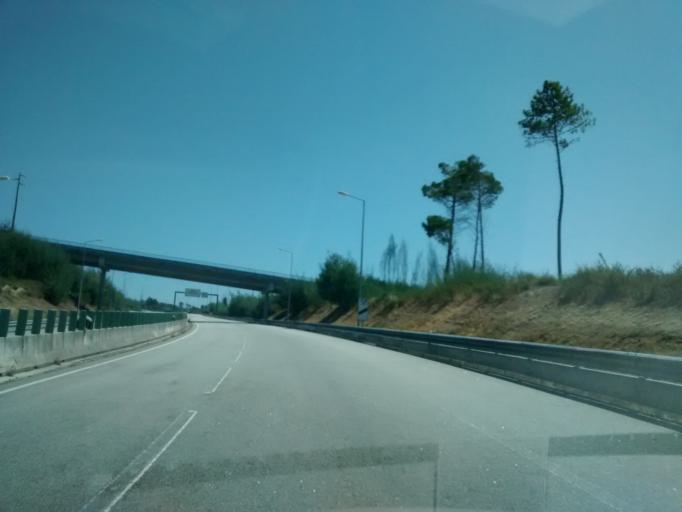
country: PT
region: Coimbra
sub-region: Tabua
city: Tabua
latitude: 40.3662
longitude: -8.0484
